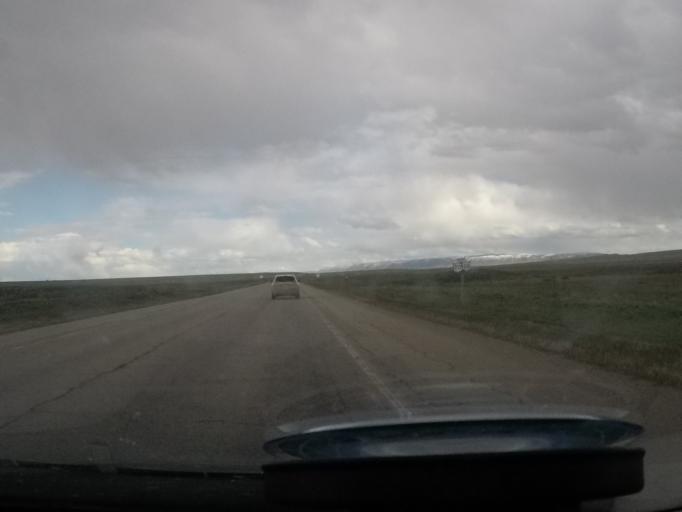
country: US
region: Wyoming
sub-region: Natrona County
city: Mills
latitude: 42.9513
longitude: -106.6360
